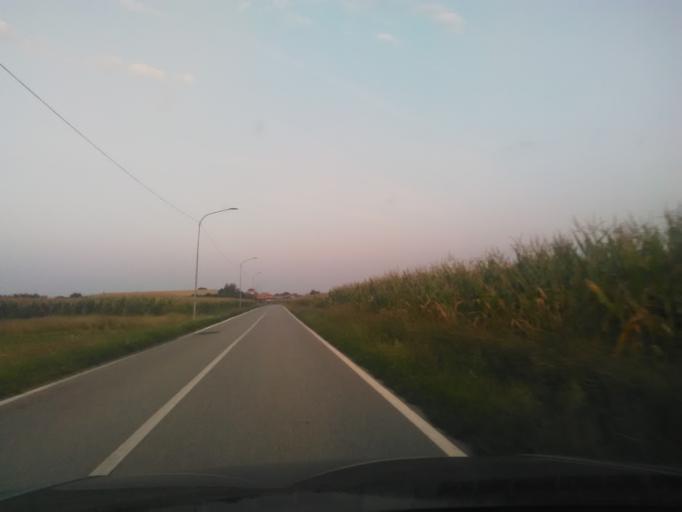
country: IT
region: Piedmont
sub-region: Provincia di Biella
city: Sandigliano
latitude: 45.5154
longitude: 8.0659
